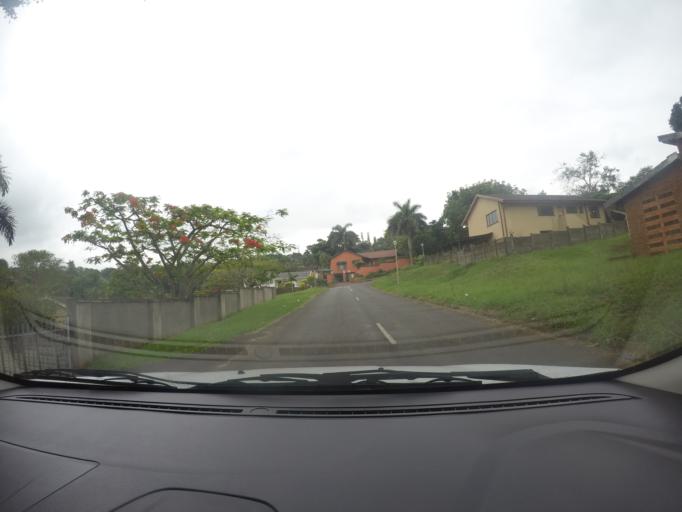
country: ZA
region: KwaZulu-Natal
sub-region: uThungulu District Municipality
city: Empangeni
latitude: -28.7587
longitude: 31.8863
